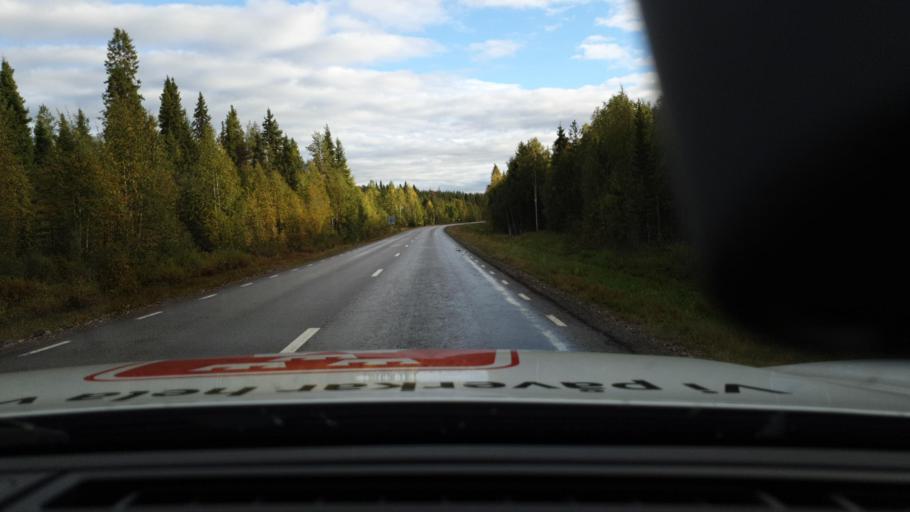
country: SE
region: Norrbotten
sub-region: Overkalix Kommun
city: OEverkalix
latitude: 66.6084
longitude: 22.7595
